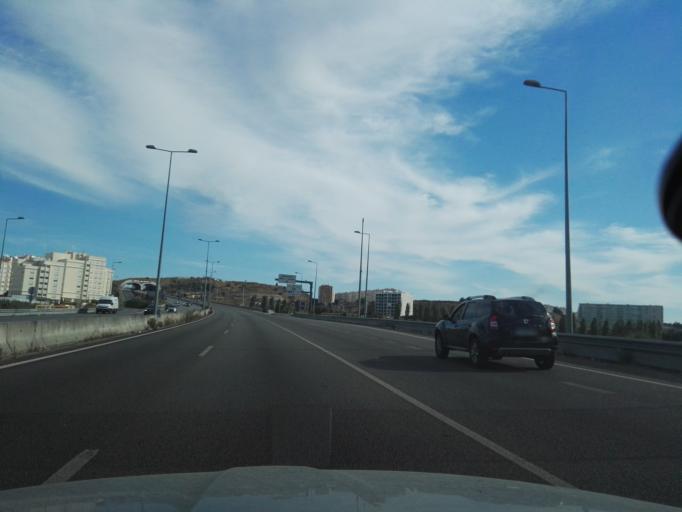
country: PT
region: Lisbon
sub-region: Odivelas
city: Olival do Basto
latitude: 38.7788
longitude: -9.1571
